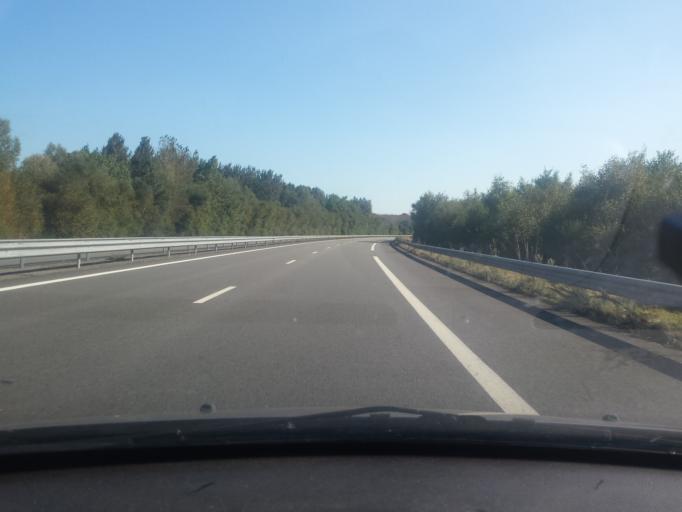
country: FR
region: Brittany
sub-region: Departement du Morbihan
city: Naizin
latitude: 47.9841
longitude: -2.8713
